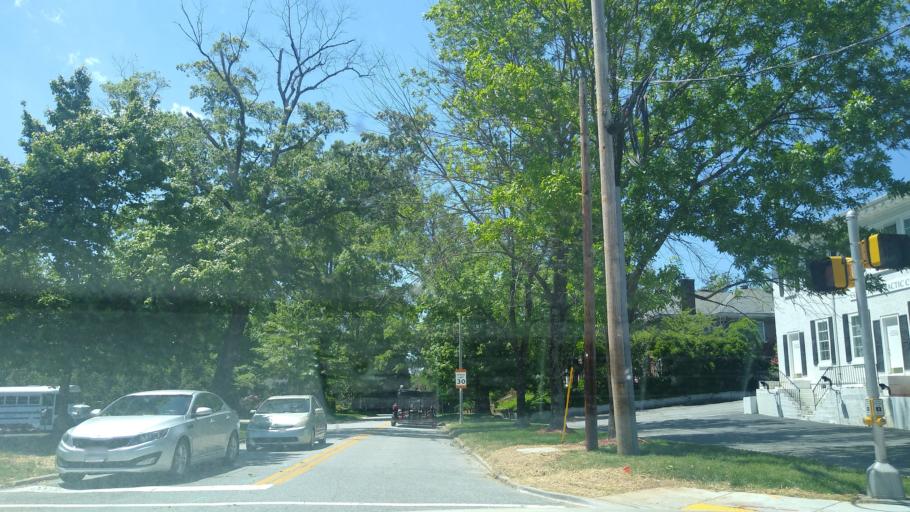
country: US
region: North Carolina
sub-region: Guilford County
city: Greensboro
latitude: 36.0861
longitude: -79.7891
